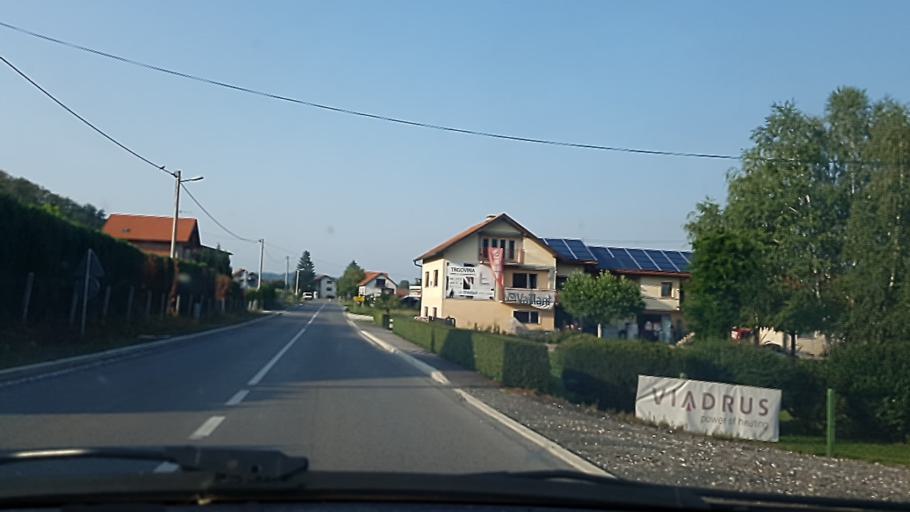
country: HR
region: Zagrebacka
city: Jakovlje
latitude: 46.0069
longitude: 15.8519
